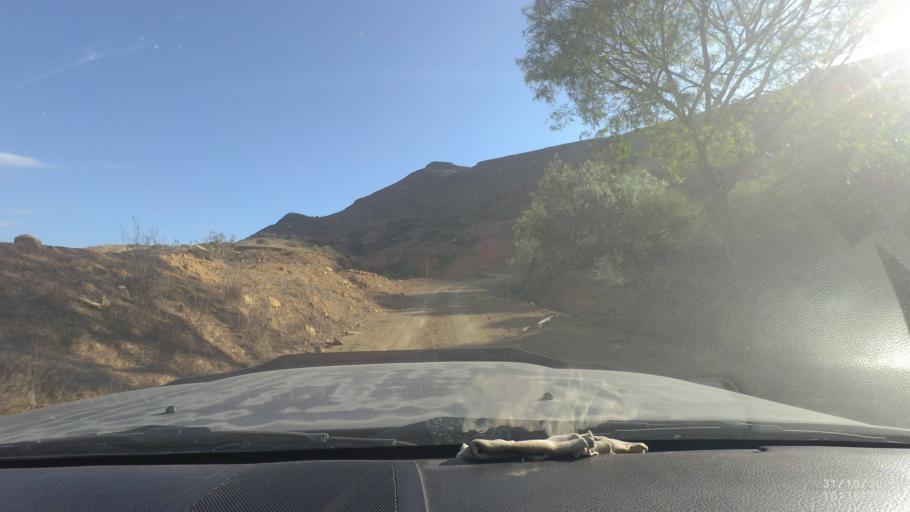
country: BO
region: Chuquisaca
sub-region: Provincia Zudanez
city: Mojocoya
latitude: -18.4578
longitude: -64.5826
